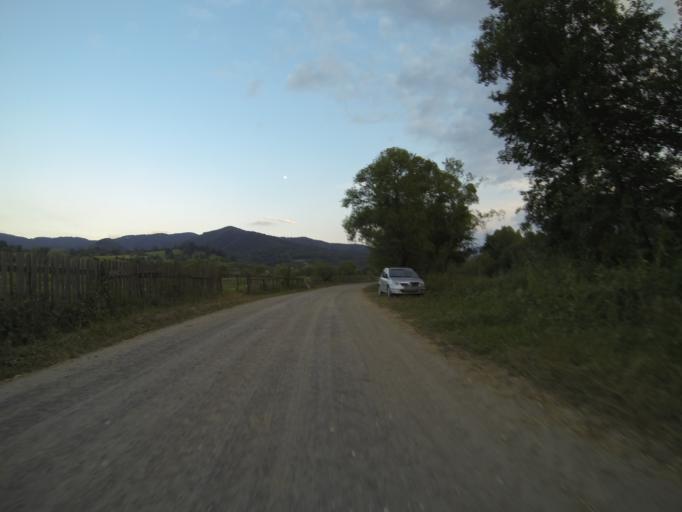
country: RO
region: Brasov
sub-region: Comuna Sinca Noua
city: Sinca Noua
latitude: 45.7109
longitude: 25.2454
